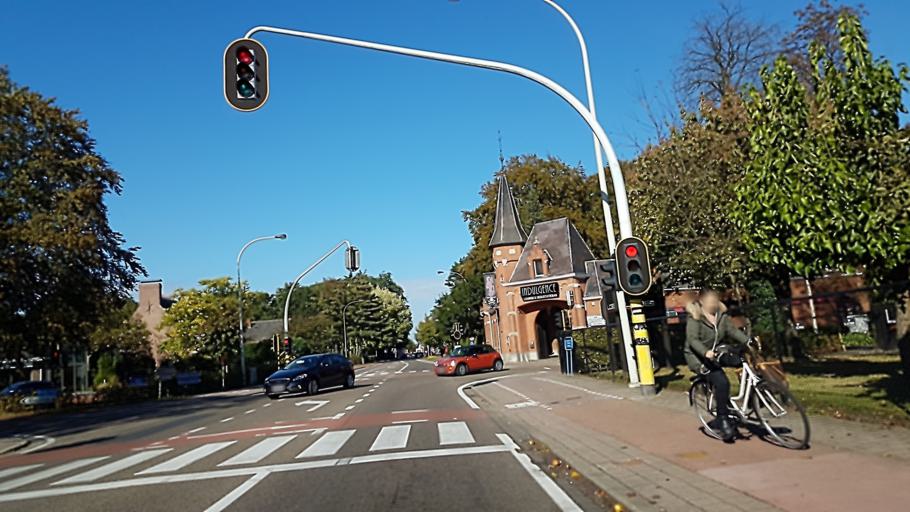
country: BE
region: Flanders
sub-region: Provincie Antwerpen
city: Kapellen
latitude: 51.3027
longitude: 4.4365
